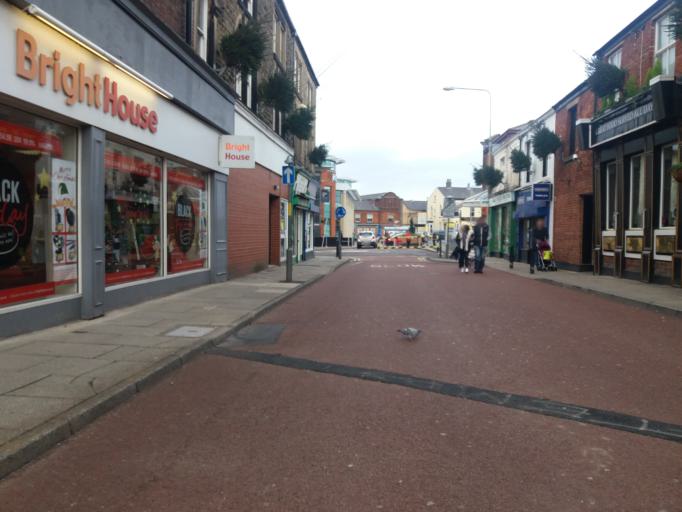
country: GB
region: England
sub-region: Lancashire
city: Chorley
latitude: 53.6534
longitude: -2.6304
